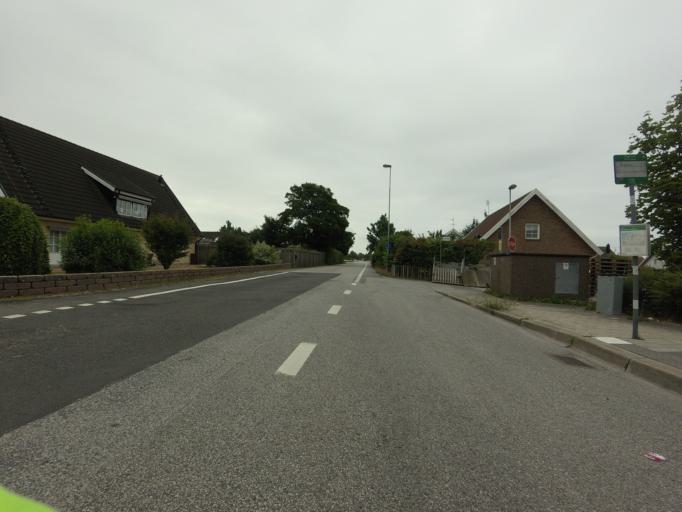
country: SE
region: Skane
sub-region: Malmo
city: Bunkeflostrand
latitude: 55.5345
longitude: 12.9220
